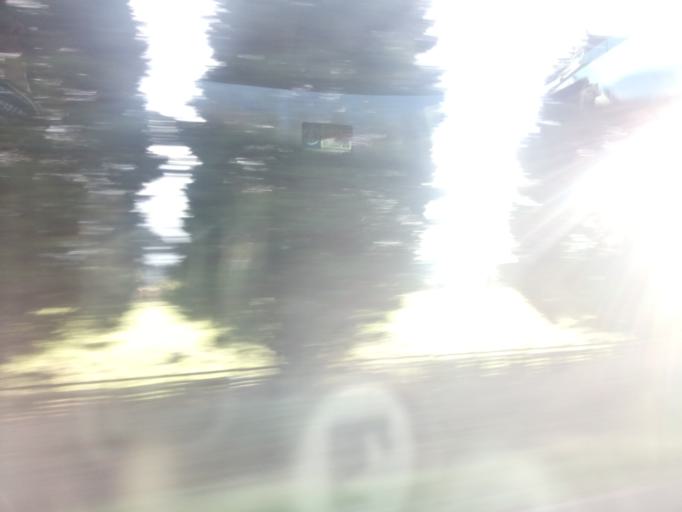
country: GB
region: England
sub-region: Somerset
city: Taunton
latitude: 51.0054
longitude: -3.0726
